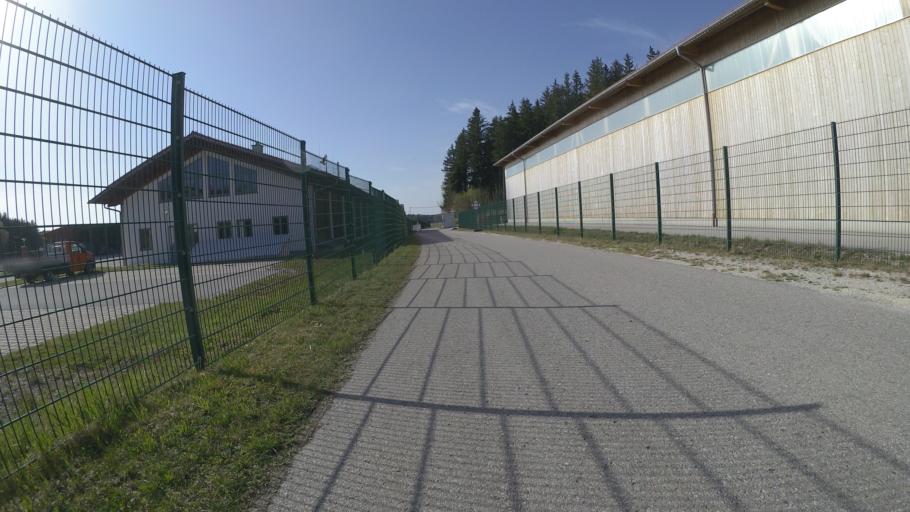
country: DE
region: Bavaria
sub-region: Upper Bavaria
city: Nussdorf
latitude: 47.9204
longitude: 12.5996
